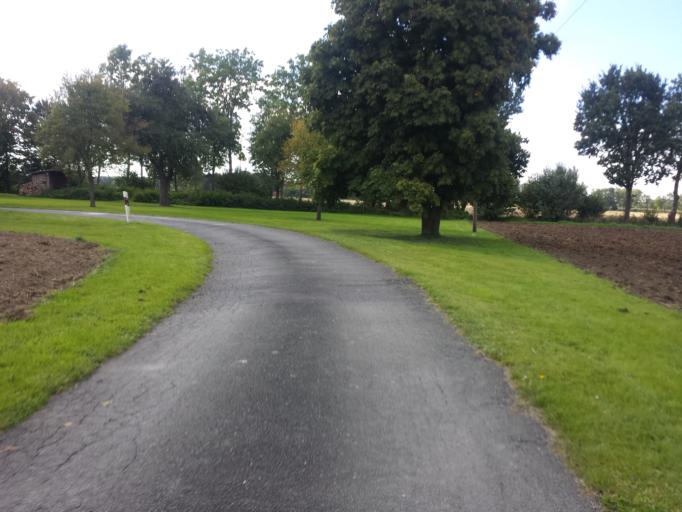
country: DE
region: North Rhine-Westphalia
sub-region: Regierungsbezirk Detmold
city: Langenberg
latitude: 51.7596
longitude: 8.3174
